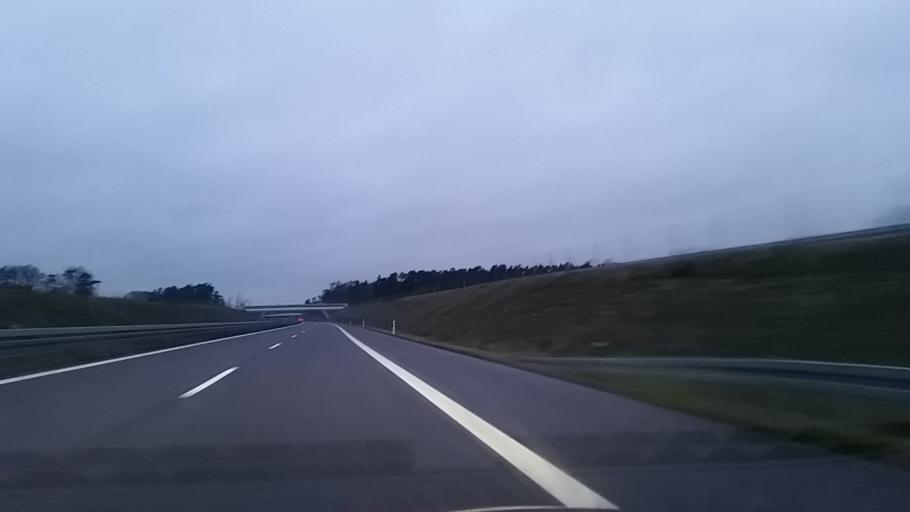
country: DE
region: Brandenburg
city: Karstadt
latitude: 53.1801
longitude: 11.6973
